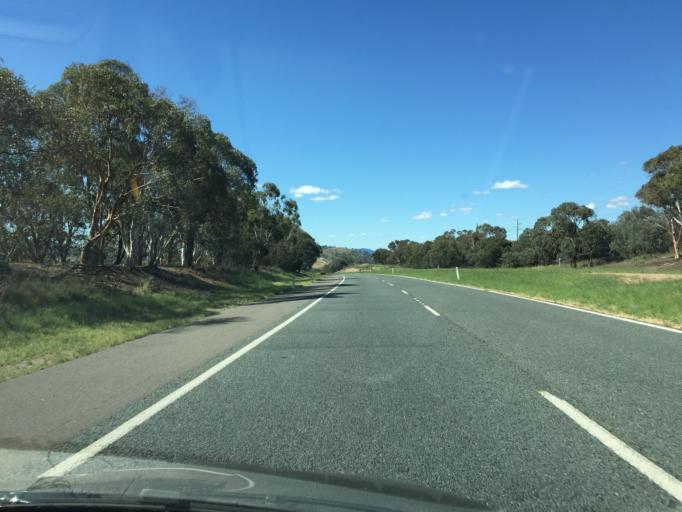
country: AU
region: Australian Capital Territory
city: Macarthur
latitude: -35.4185
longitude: 149.1442
